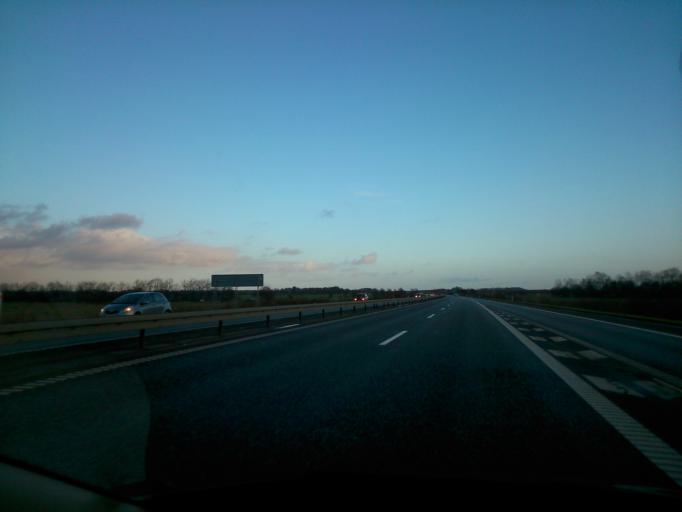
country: DK
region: Central Jutland
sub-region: Herning Kommune
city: Hammerum
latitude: 56.1201
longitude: 9.0550
